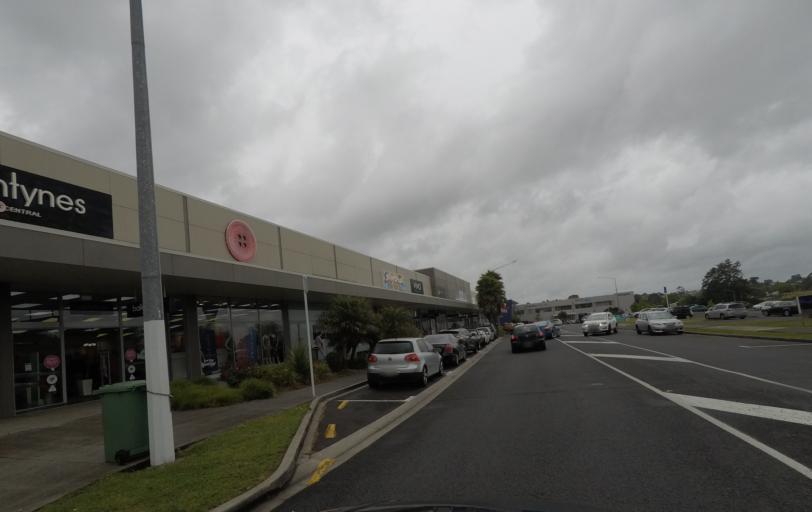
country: NZ
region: Auckland
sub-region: Auckland
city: Rosebank
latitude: -36.8227
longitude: 174.6116
